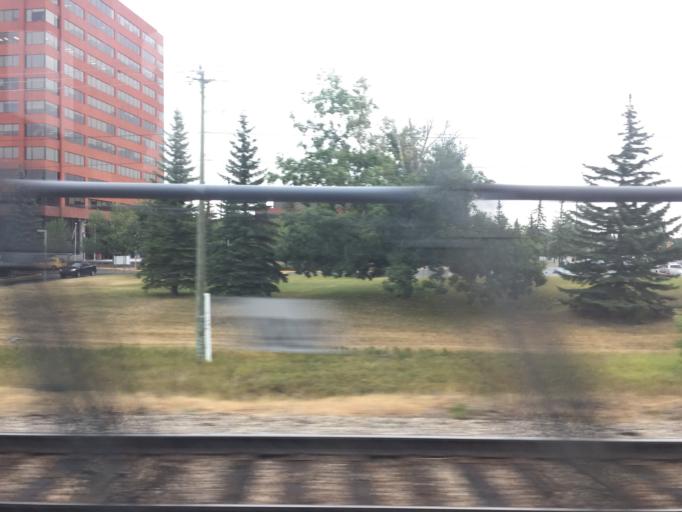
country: CA
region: Alberta
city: Calgary
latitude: 50.9581
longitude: -114.0753
